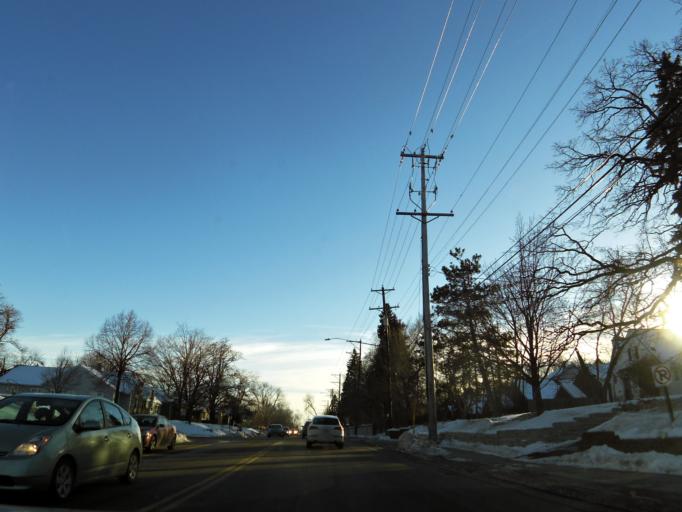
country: US
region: Minnesota
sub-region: Hennepin County
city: Saint Louis Park
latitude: 44.9201
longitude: -93.3292
